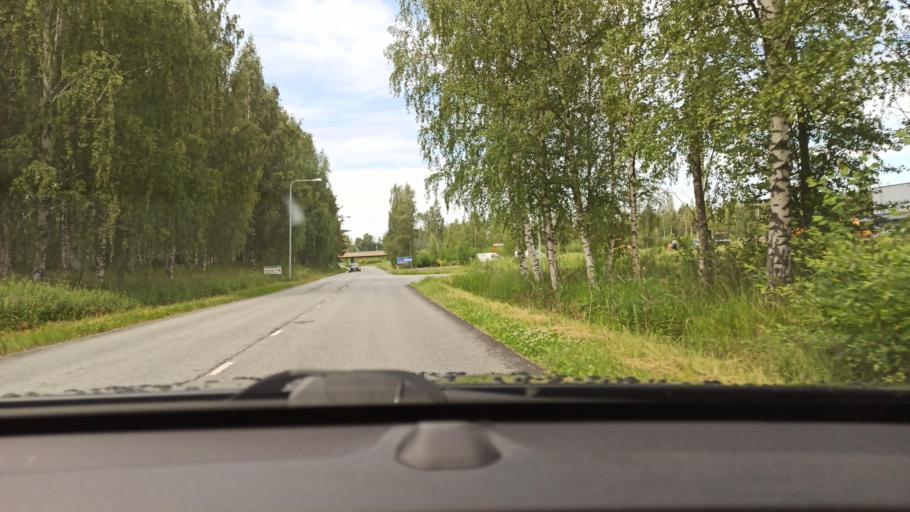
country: FI
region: Satakunta
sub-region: Pori
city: Pori
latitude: 61.5107
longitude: 21.7737
